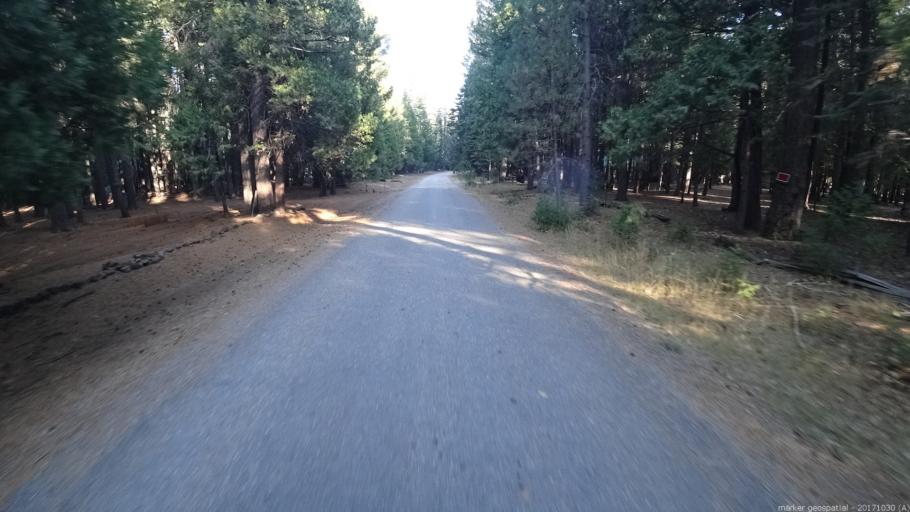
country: US
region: California
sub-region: Shasta County
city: Shingletown
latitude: 40.5586
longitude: -121.7340
